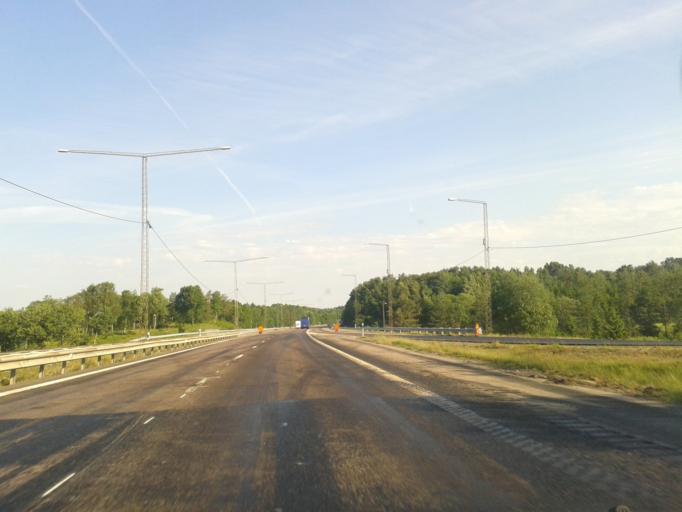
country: SE
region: Vaestra Goetaland
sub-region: Kungalvs Kommun
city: Kode
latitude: 57.9444
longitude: 11.8574
